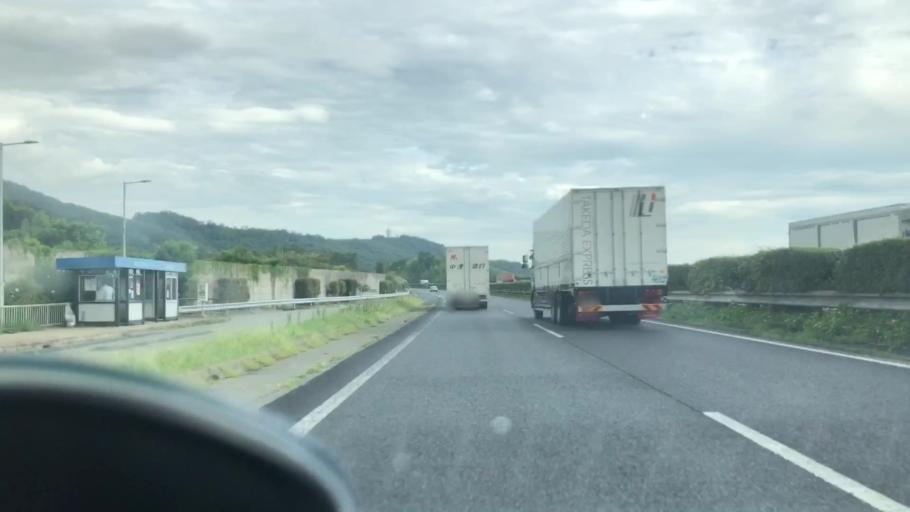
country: JP
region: Hyogo
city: Ono
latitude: 34.9353
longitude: 134.8367
